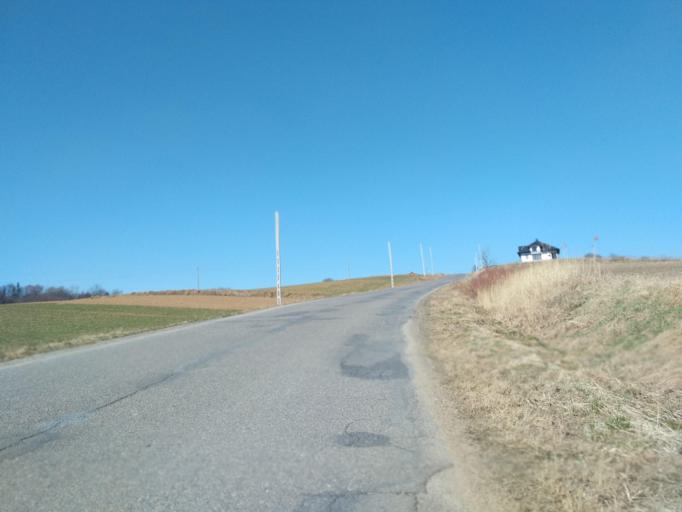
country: PL
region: Subcarpathian Voivodeship
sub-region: Powiat debicki
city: Brzostek
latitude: 49.9416
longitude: 21.4364
